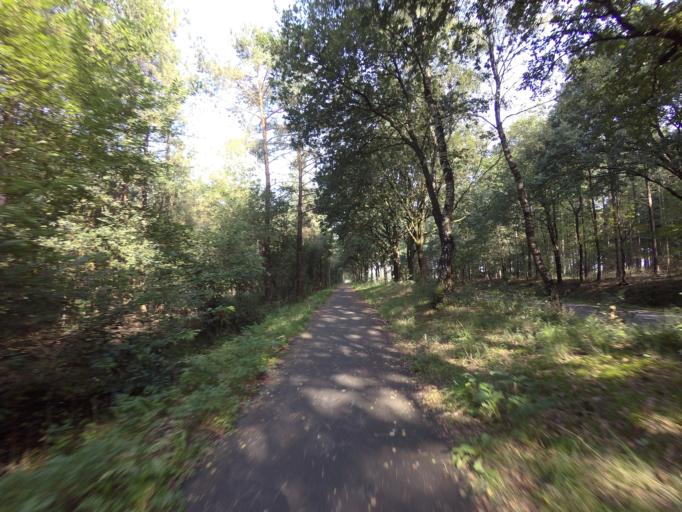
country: DE
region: Lower Saxony
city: Wielen
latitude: 52.5419
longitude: 6.6987
